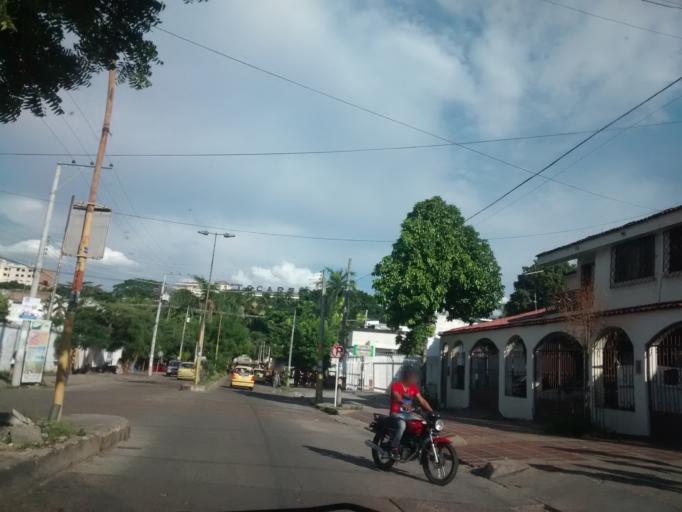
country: CO
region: Cundinamarca
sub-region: Girardot
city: Girardot City
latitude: 4.2973
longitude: -74.8040
